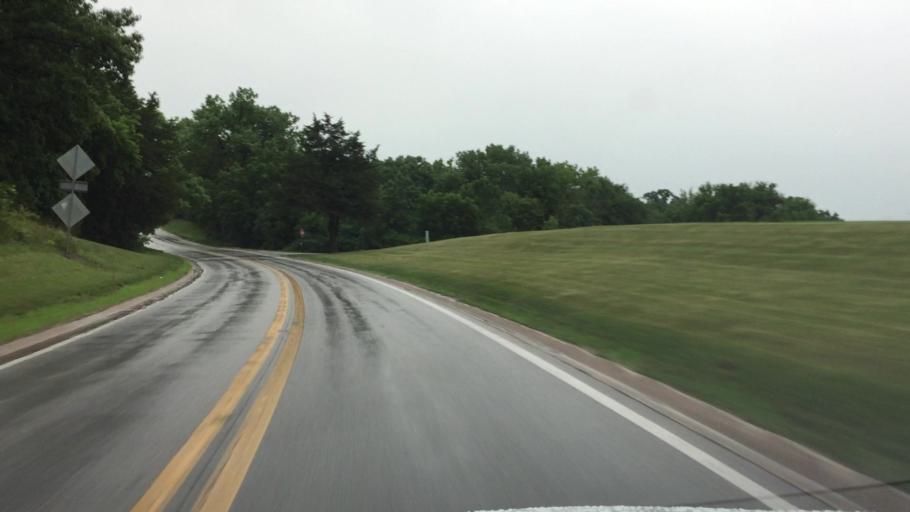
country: US
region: Illinois
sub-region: Hancock County
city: Carthage
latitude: 40.4242
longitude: -91.1368
